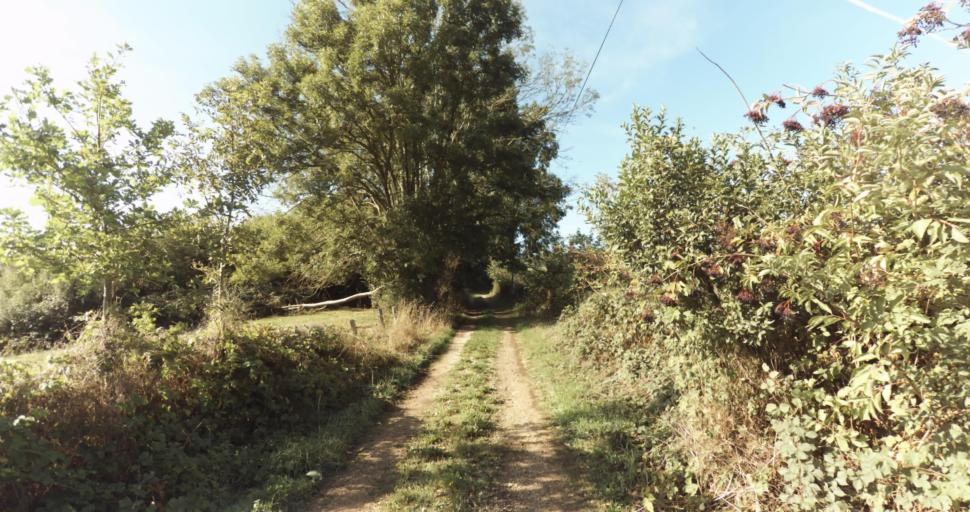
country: FR
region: Lower Normandy
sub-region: Departement de l'Orne
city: Vimoutiers
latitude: 48.9357
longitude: 0.2996
